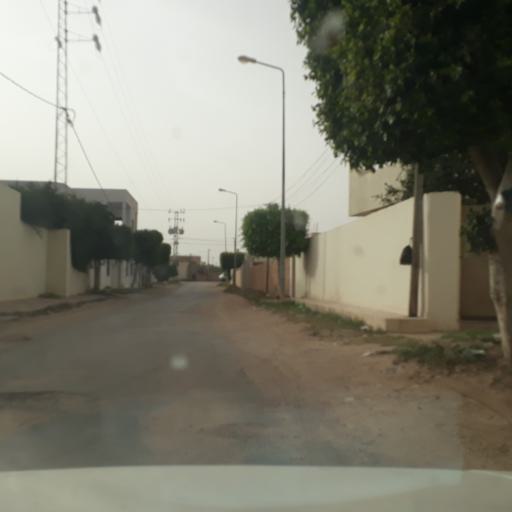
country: TN
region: Safaqis
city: Al Qarmadah
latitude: 34.8150
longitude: 10.7684
